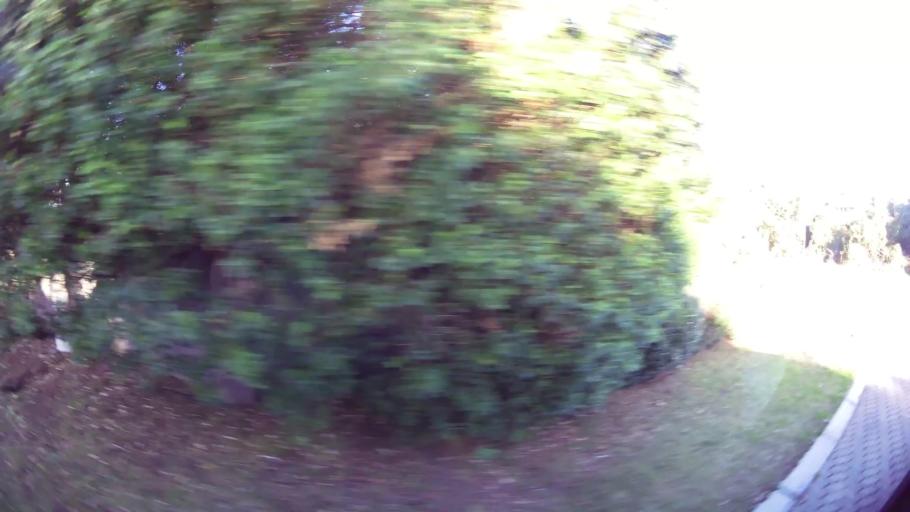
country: ZA
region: Western Cape
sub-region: Eden District Municipality
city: George
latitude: -33.9982
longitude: 22.6211
